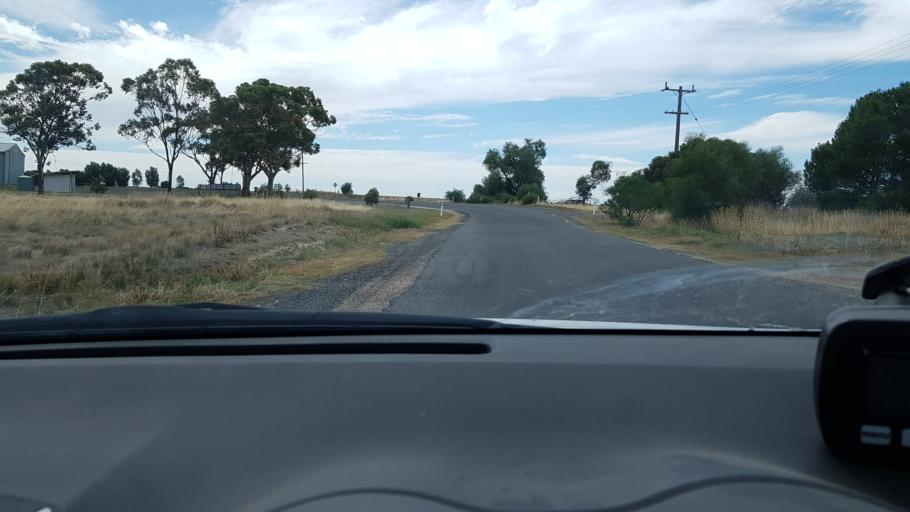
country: AU
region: Victoria
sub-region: Horsham
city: Horsham
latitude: -36.7277
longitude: 141.7813
